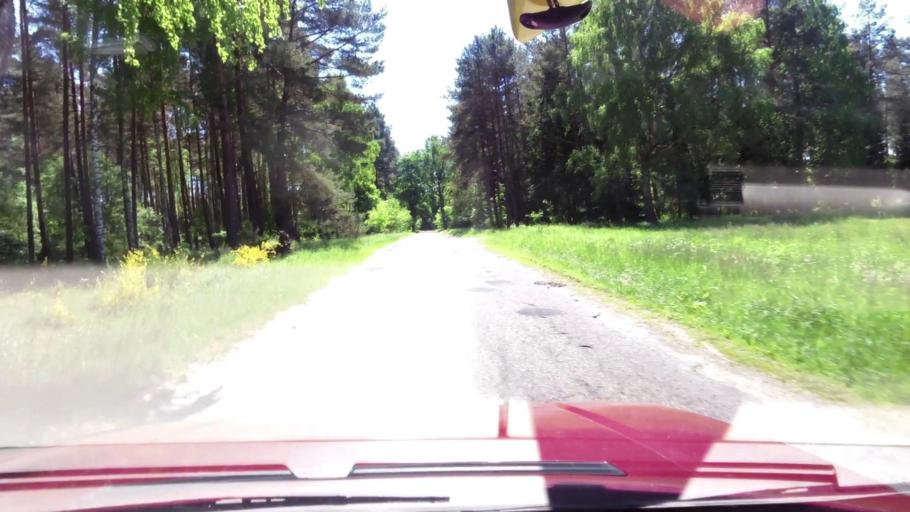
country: PL
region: West Pomeranian Voivodeship
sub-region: Powiat koszalinski
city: Bobolice
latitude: 54.0463
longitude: 16.5913
